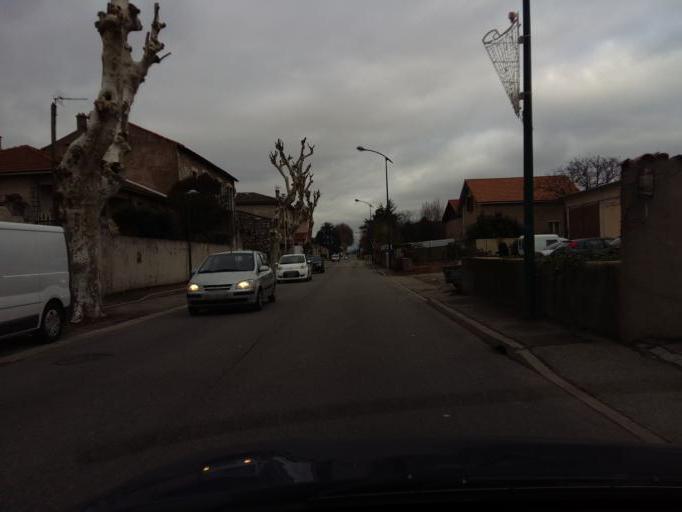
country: FR
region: Rhone-Alpes
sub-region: Departement de l'Ardeche
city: Cornas
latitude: 44.9630
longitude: 4.8487
